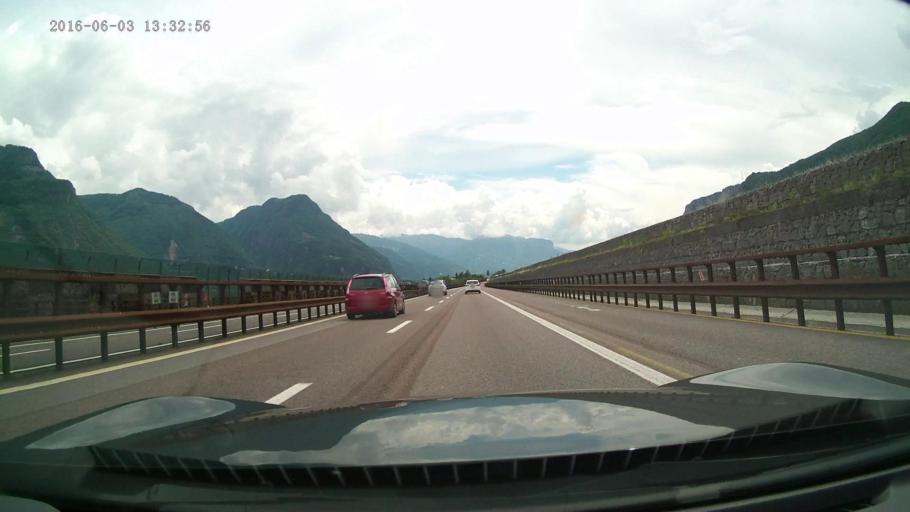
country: IT
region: Trentino-Alto Adige
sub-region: Bolzano
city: Vadena
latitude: 46.4271
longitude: 11.3157
